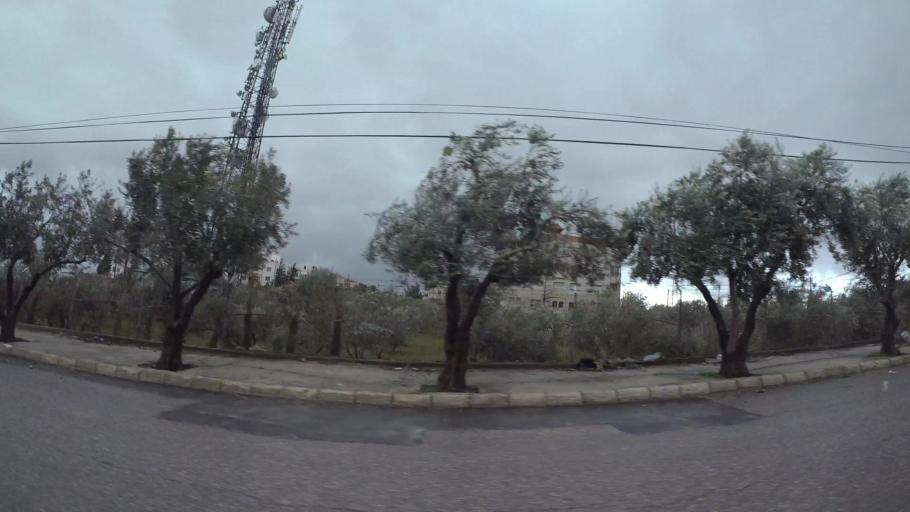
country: JO
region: Amman
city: Al Jubayhah
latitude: 32.0364
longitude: 35.8609
